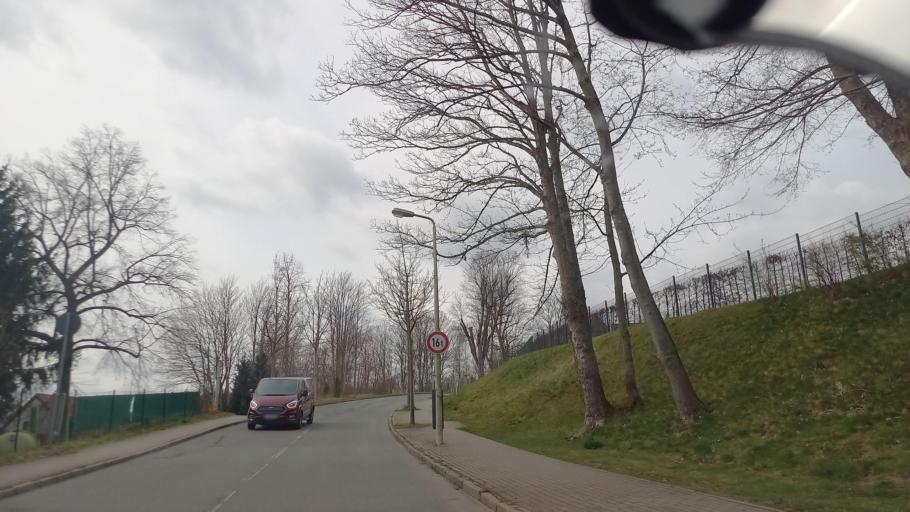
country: DE
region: Saxony
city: Zwickau
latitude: 50.6993
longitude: 12.4955
